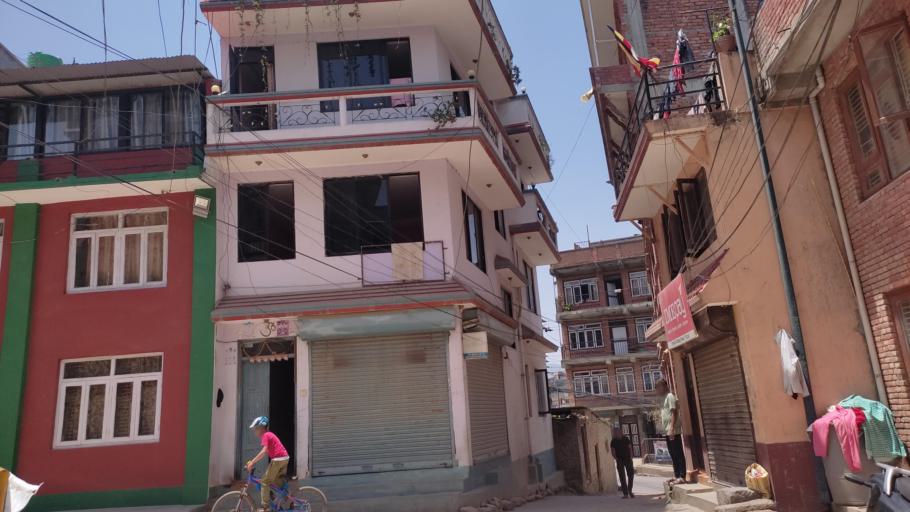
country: NP
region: Central Region
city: Kirtipur
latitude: 27.6733
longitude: 85.2760
